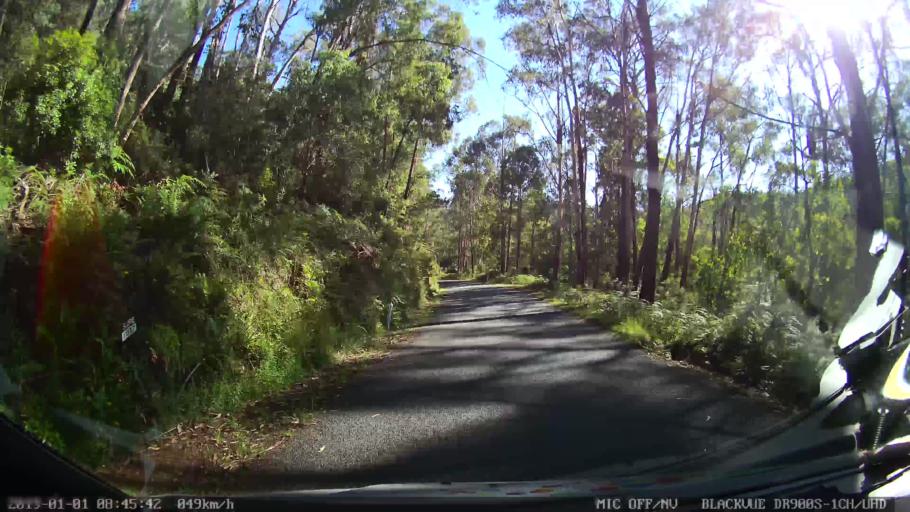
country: AU
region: New South Wales
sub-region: Snowy River
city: Jindabyne
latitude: -36.3039
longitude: 148.1897
